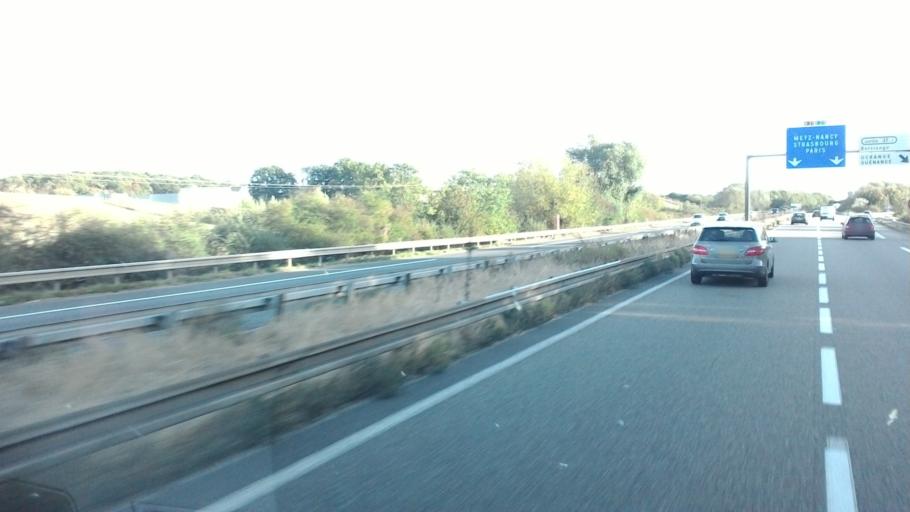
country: FR
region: Lorraine
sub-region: Departement de la Moselle
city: Bertrange
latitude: 49.3055
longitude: 6.1833
